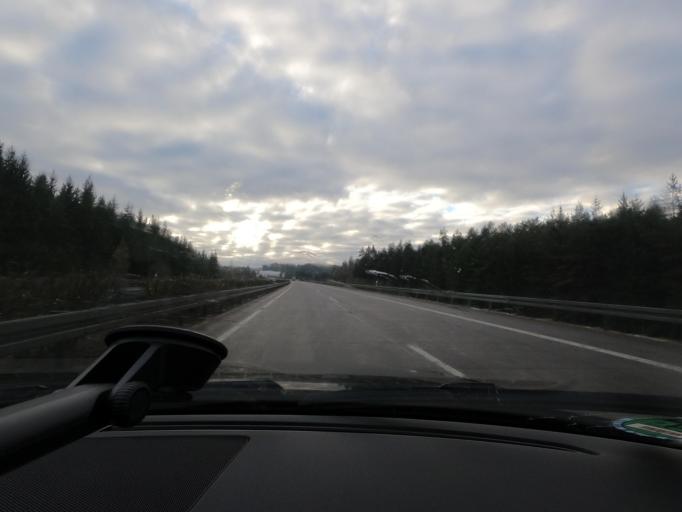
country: DE
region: Thuringia
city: Schleusingen
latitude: 50.4786
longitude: 10.8203
